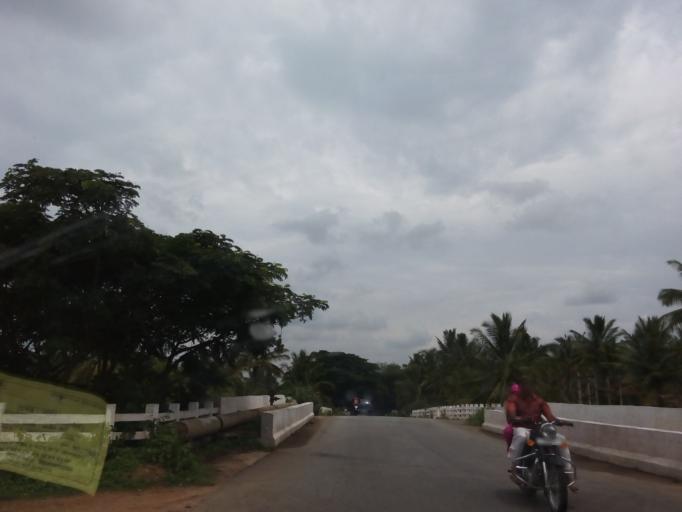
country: IN
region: Karnataka
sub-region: Hassan
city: Shravanabelagola
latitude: 12.8726
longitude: 76.4475
